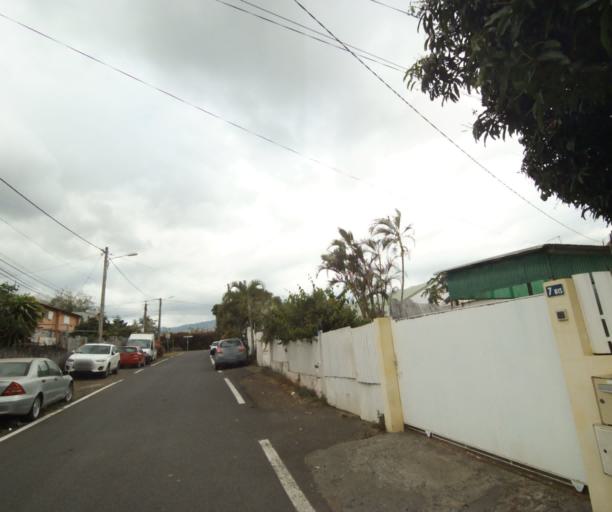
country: RE
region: Reunion
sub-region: Reunion
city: Saint-Paul
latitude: -20.9870
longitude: 55.2994
